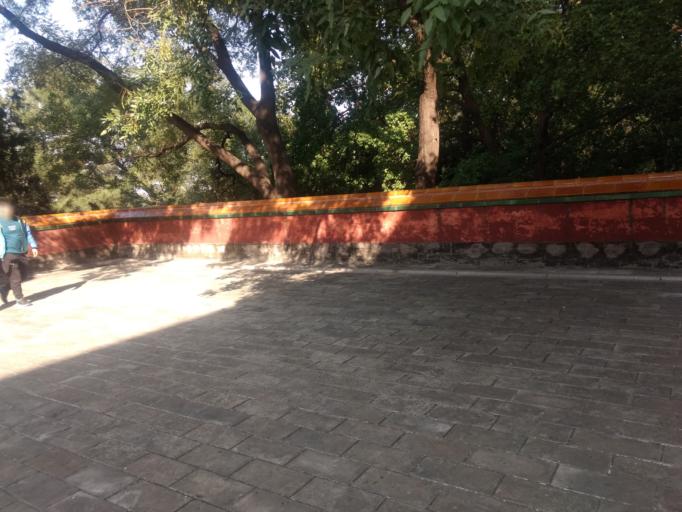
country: CN
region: Beijing
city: Haidian
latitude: 39.9990
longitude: 116.2690
